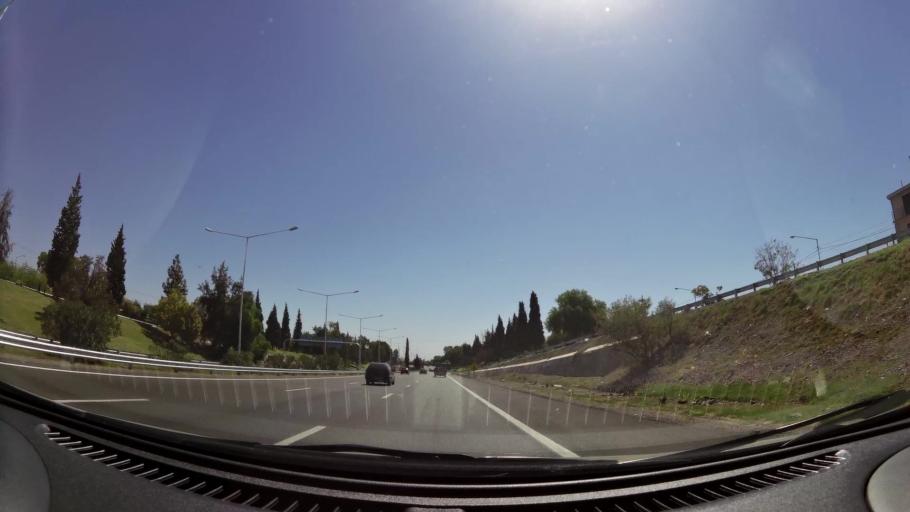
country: AR
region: Mendoza
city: Mendoza
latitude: -32.9039
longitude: -68.8198
